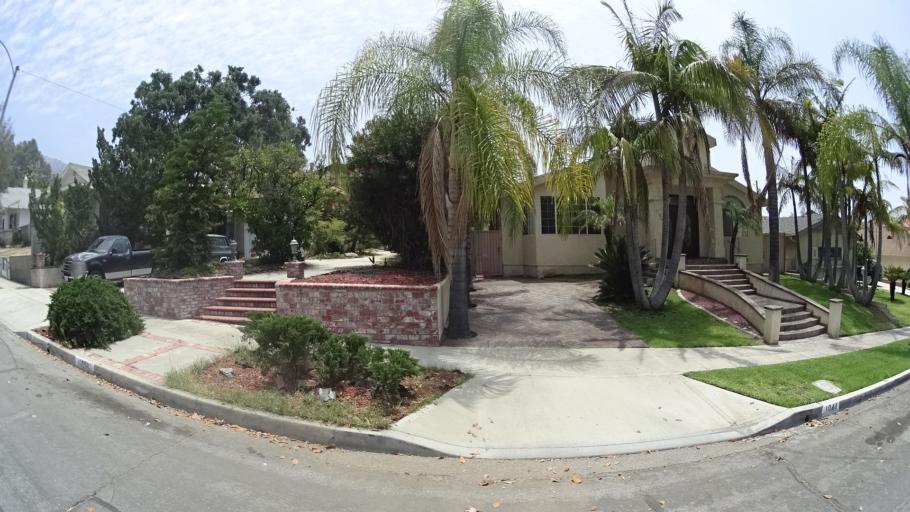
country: US
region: California
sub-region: Los Angeles County
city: Burbank
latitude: 34.1928
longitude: -118.2996
